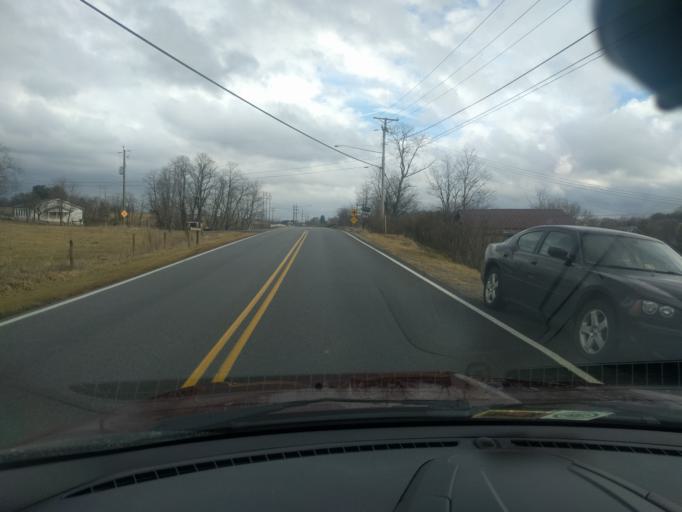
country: US
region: Virginia
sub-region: Pulaski County
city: Pulaski
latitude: 37.0631
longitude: -80.7290
